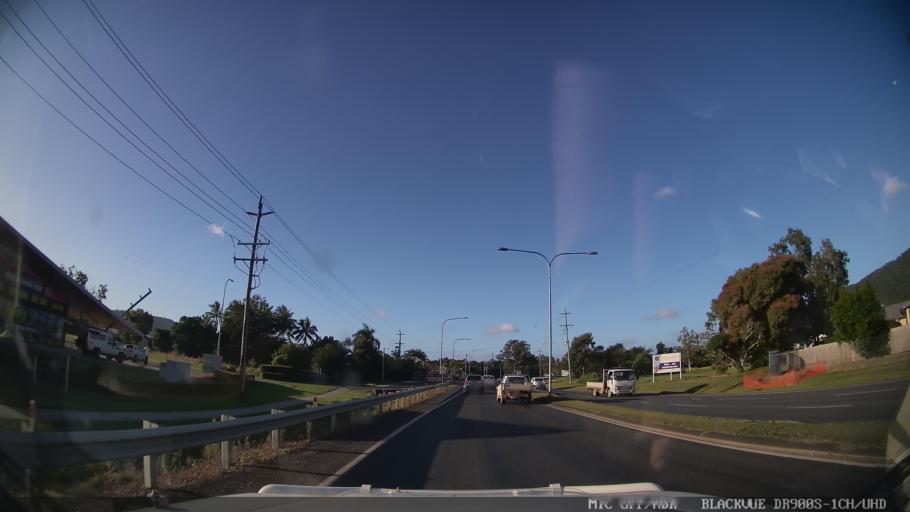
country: AU
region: Queensland
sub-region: Whitsunday
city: Proserpine
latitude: -20.2886
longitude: 148.6779
